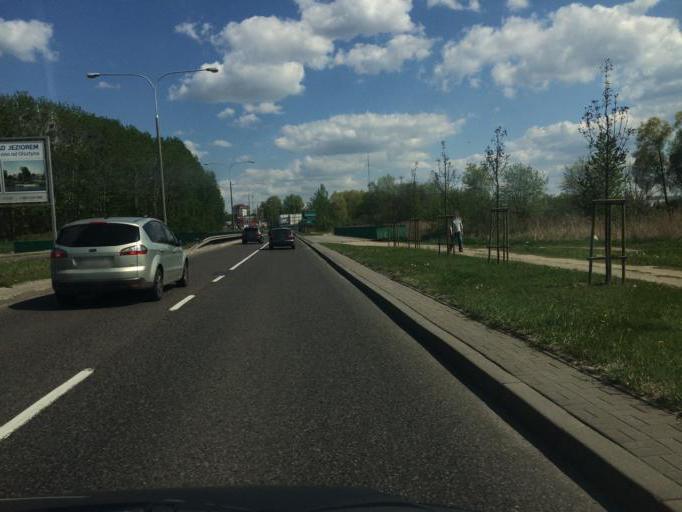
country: PL
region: Warmian-Masurian Voivodeship
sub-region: Olsztyn
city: Kortowo
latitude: 53.7656
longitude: 20.4758
